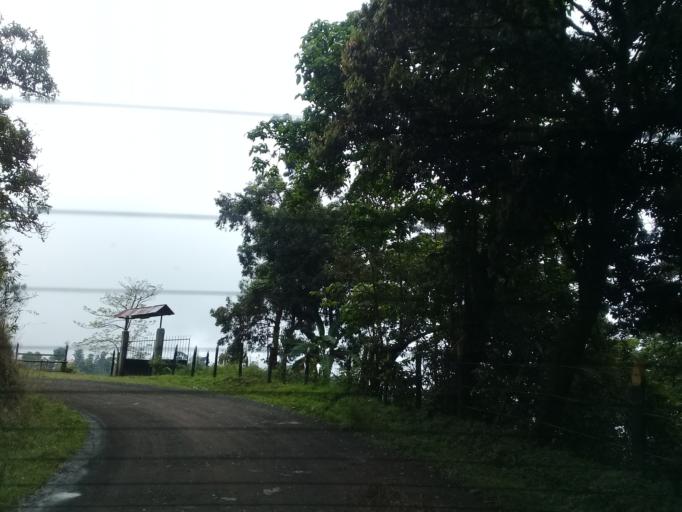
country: CO
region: Cundinamarca
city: Quipile
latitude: 4.7216
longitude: -74.5561
